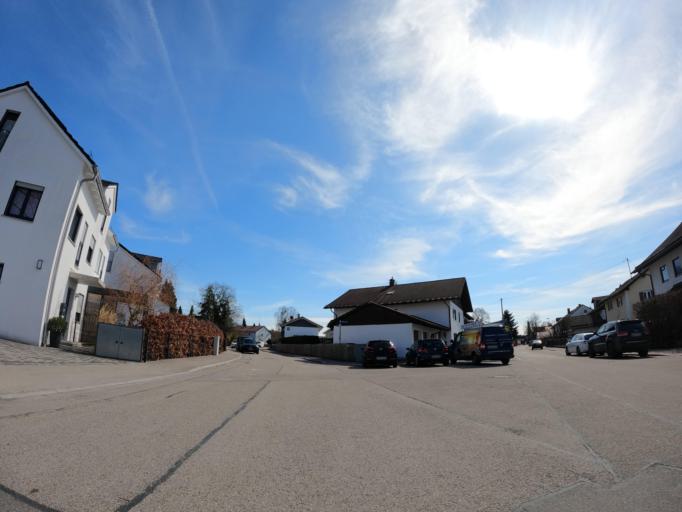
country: DE
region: Bavaria
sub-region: Upper Bavaria
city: Hohenkirchen-Siegertsbrunn
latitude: 48.0212
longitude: 11.7036
